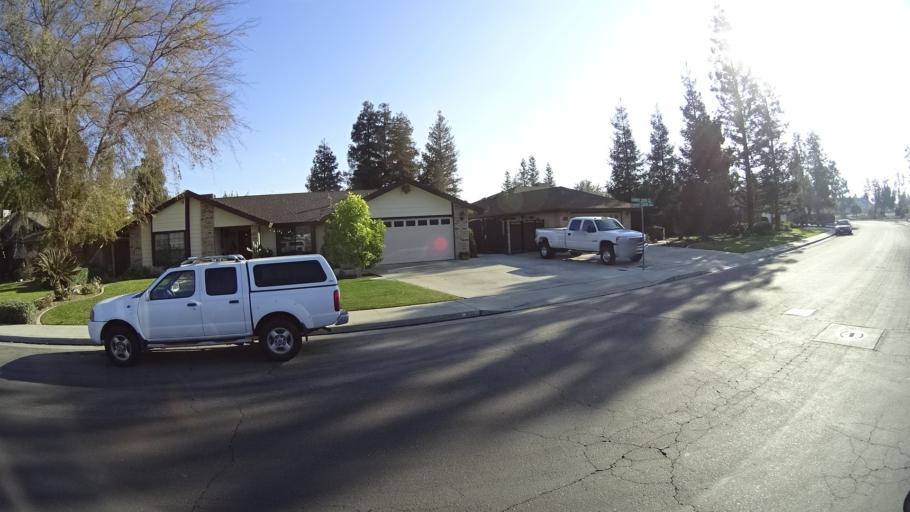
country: US
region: California
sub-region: Kern County
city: Greenacres
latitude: 35.3272
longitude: -119.1020
